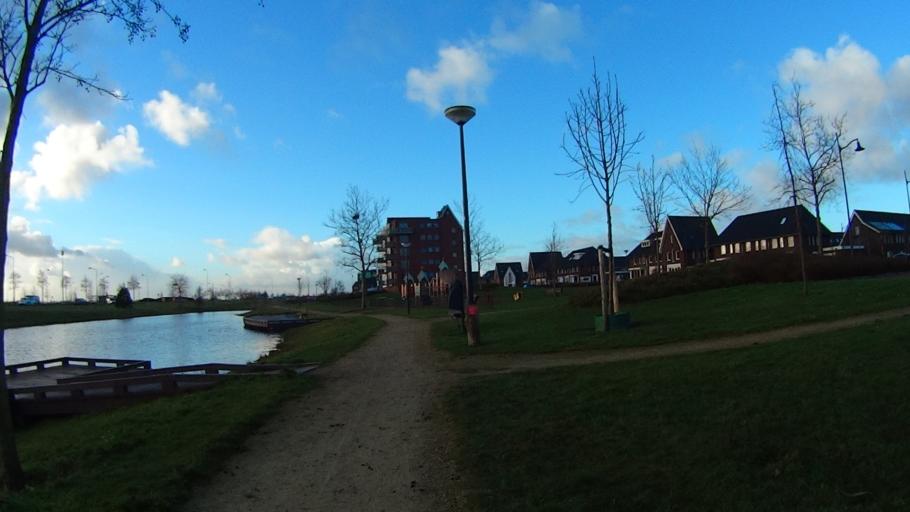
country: NL
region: Gelderland
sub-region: Gemeente Nijkerk
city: Nijkerk
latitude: 52.2103
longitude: 5.4587
